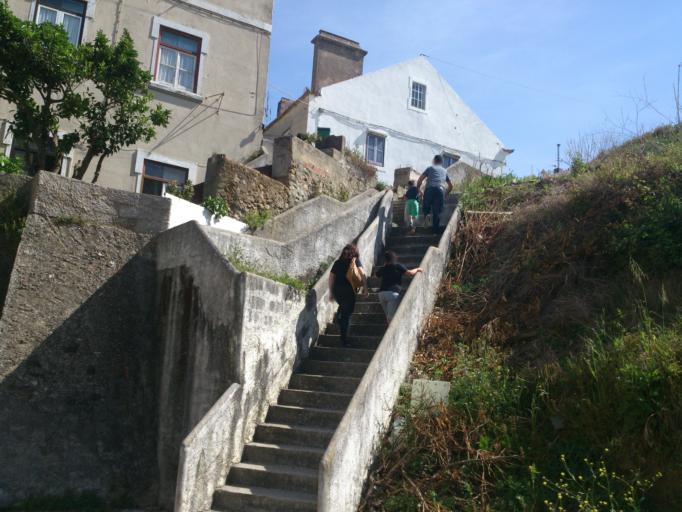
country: PT
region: Lisbon
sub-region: Mafra
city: Mafra
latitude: 38.9341
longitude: -9.3279
